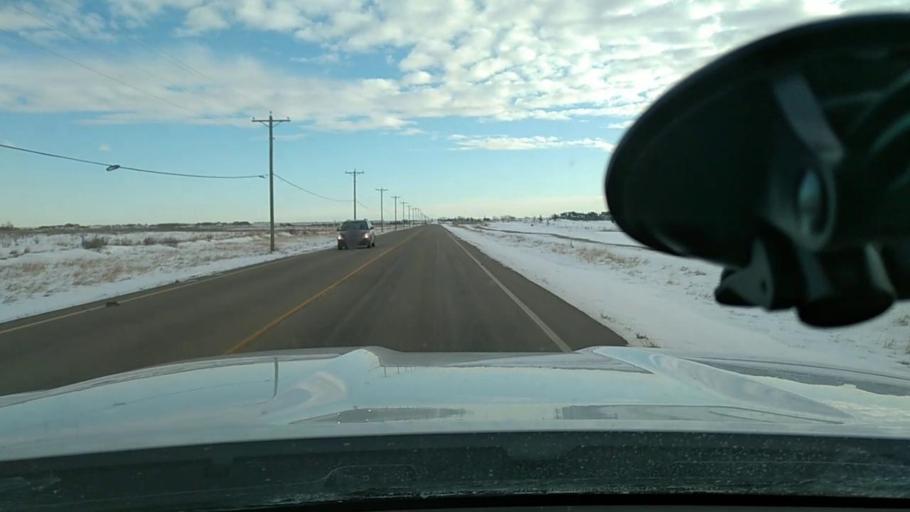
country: CA
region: Alberta
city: Chestermere
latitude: 50.9651
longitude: -113.6744
